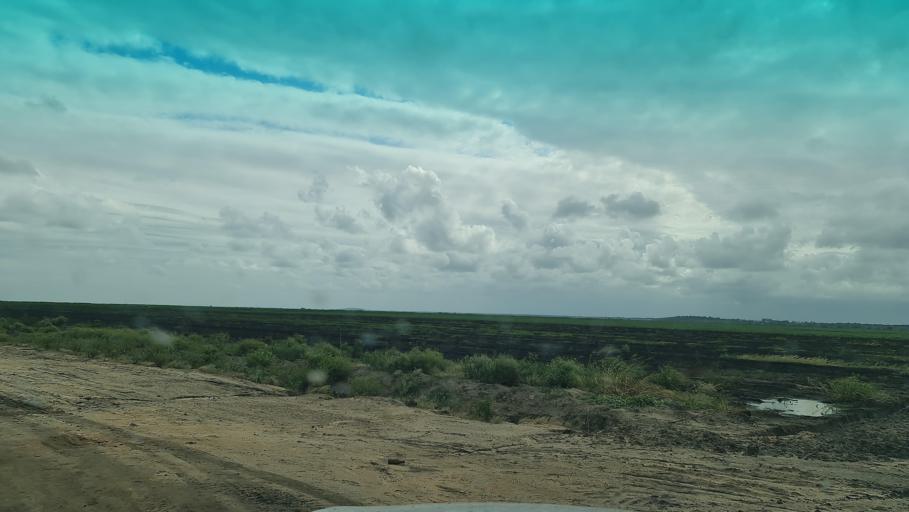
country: MZ
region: Maputo
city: Manhica
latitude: -25.4376
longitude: 32.8407
